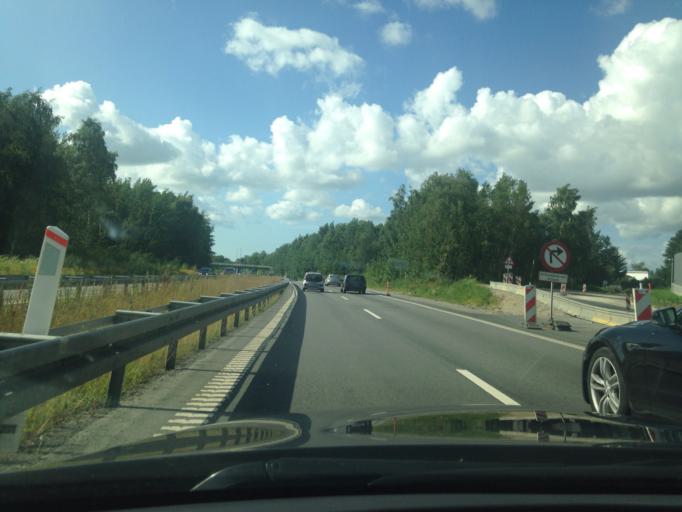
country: DK
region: Capital Region
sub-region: Horsholm Kommune
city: Horsholm
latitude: 55.8573
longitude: 12.4963
